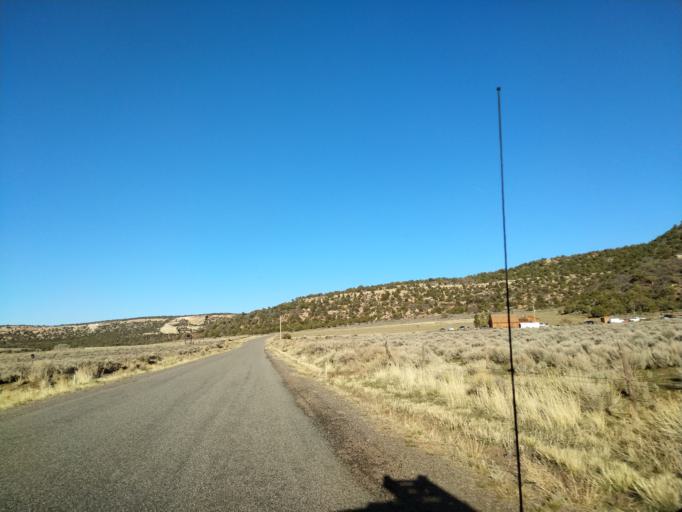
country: US
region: Colorado
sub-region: Mesa County
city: Loma
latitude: 38.9572
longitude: -109.0204
